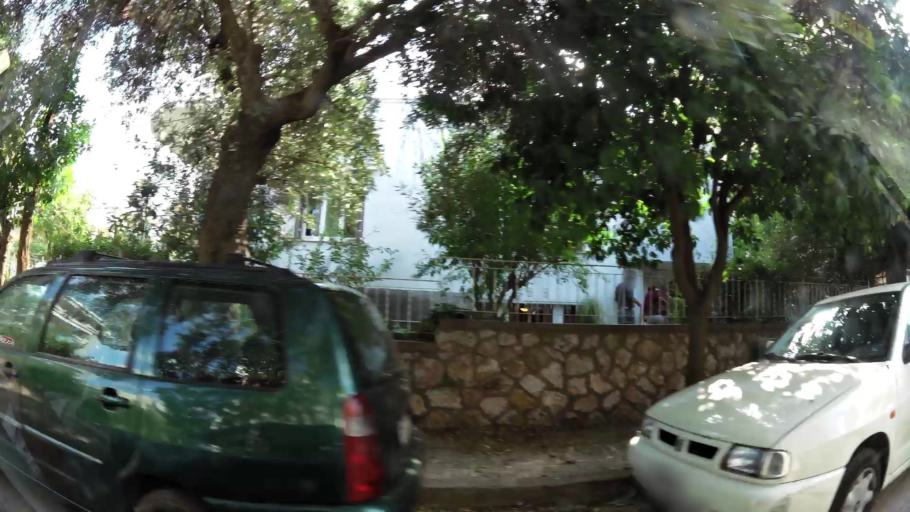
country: GR
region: Attica
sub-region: Nomarchia Athinas
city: Cholargos
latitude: 37.9949
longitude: 23.7946
